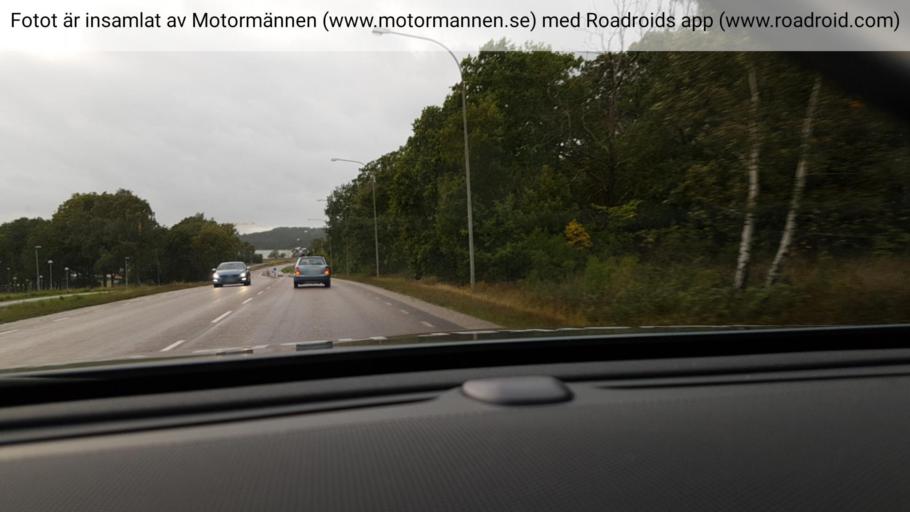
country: SE
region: Vaestra Goetaland
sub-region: Stenungsunds Kommun
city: Stenungsund
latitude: 58.0576
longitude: 11.8325
